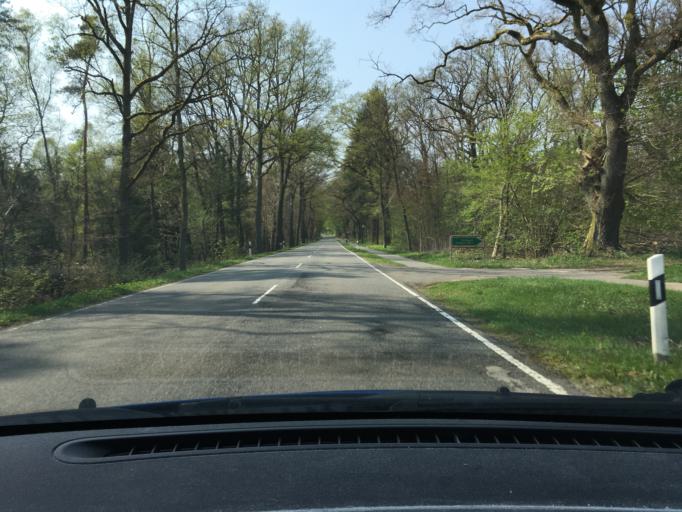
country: DE
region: Lower Saxony
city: Fassberg
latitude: 52.8704
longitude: 10.2299
